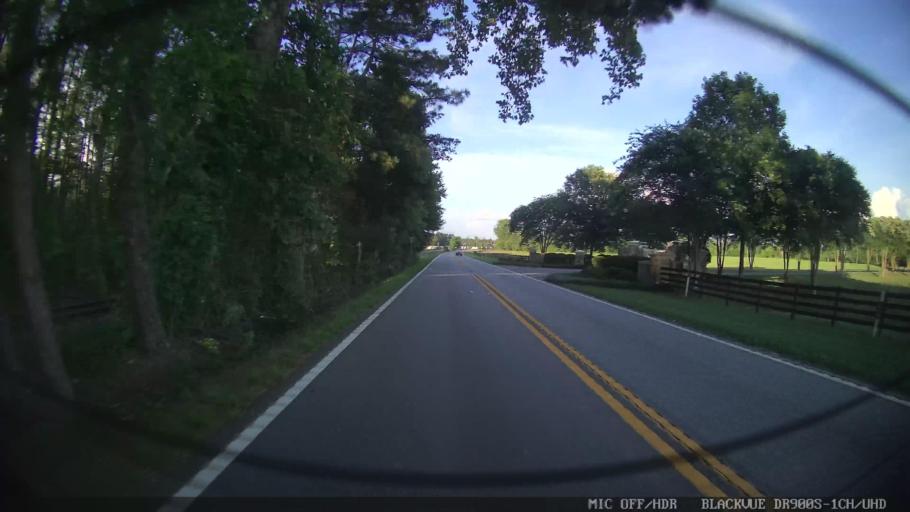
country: US
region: Georgia
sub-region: Monroe County
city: Forsyth
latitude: 32.9549
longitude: -83.8348
